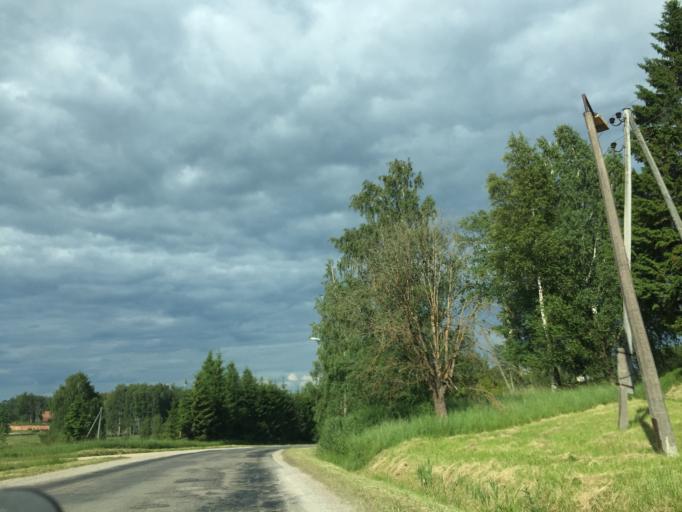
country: LV
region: Skriveri
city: Skriveri
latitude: 56.8431
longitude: 25.1472
